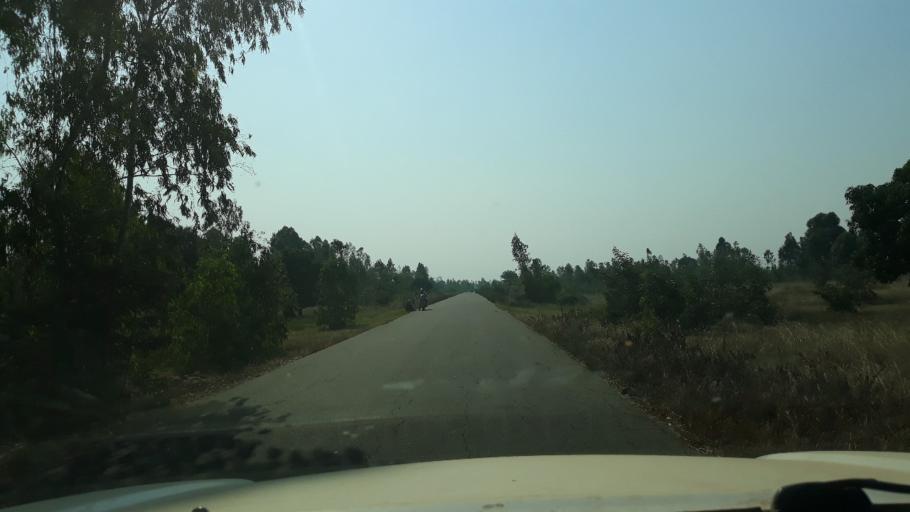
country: BI
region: Cibitoke
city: Cibitoke
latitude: -2.9535
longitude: 29.0745
